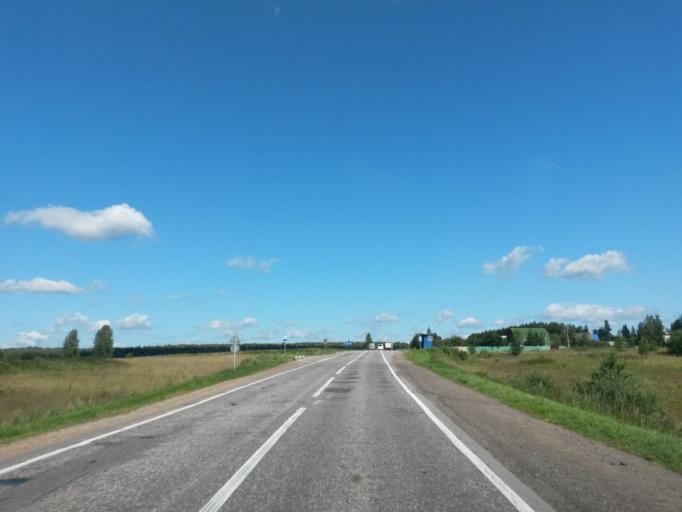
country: RU
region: Jaroslavl
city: Krasnyye Tkachi
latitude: 57.4589
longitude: 39.9095
